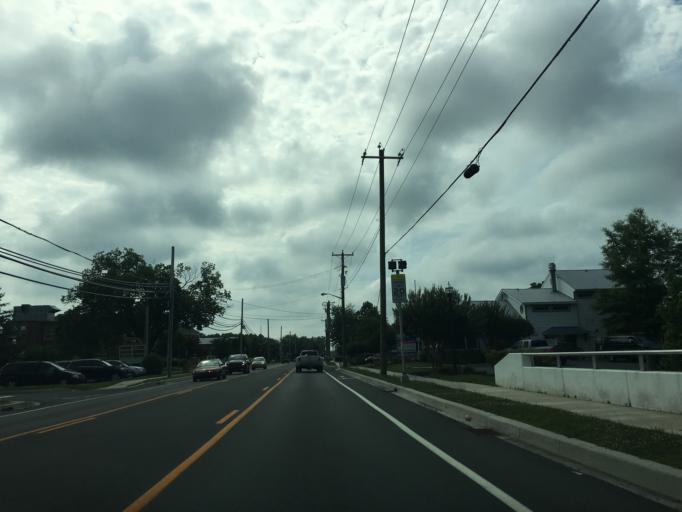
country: US
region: Delaware
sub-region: Sussex County
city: Ocean View
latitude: 38.5454
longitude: -75.0979
